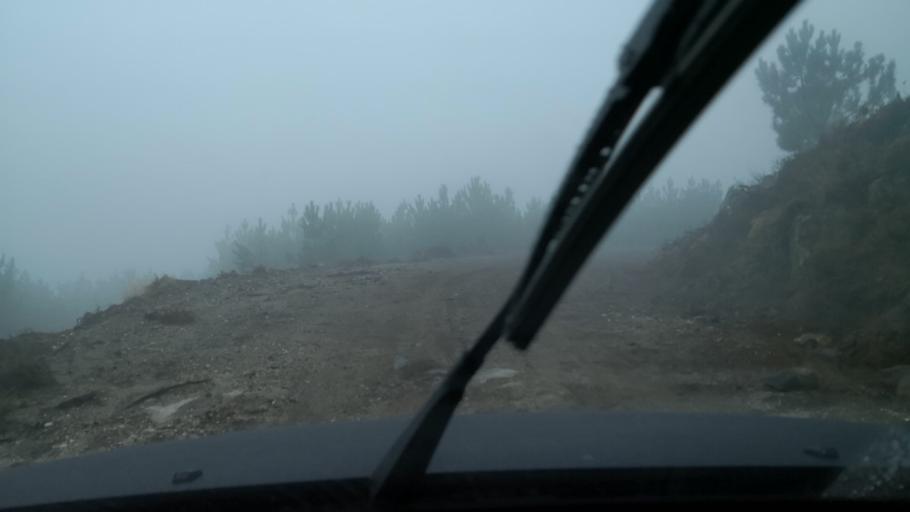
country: PT
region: Vila Real
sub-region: Vila Real
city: Vila Real
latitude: 41.3711
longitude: -7.7448
